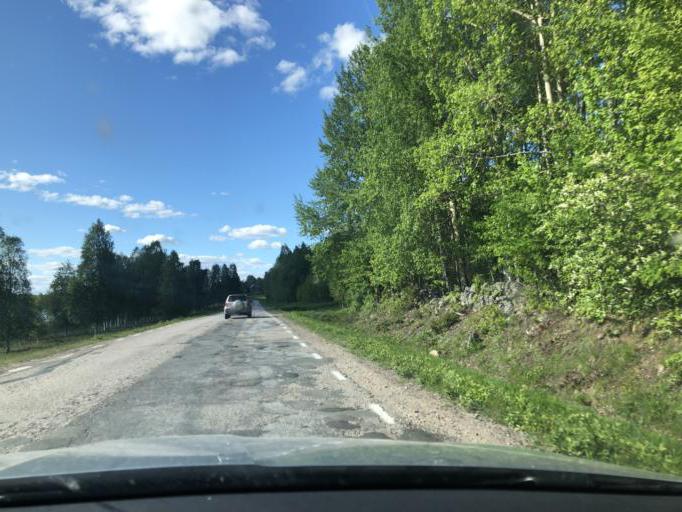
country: SE
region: Norrbotten
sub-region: Kalix Kommun
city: Kalix
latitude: 65.9949
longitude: 23.1491
